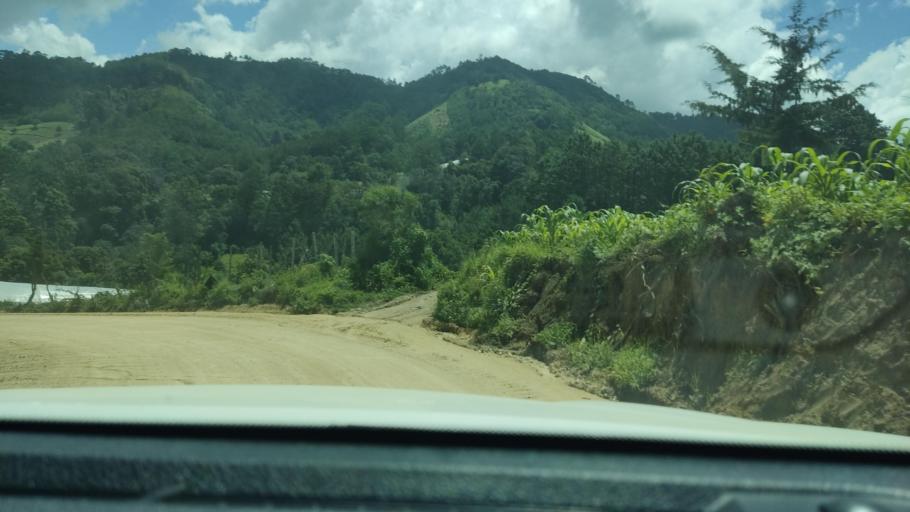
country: GT
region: Chimaltenango
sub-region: Municipio de San Juan Comalapa
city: Comalapa
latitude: 14.7647
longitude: -90.8835
